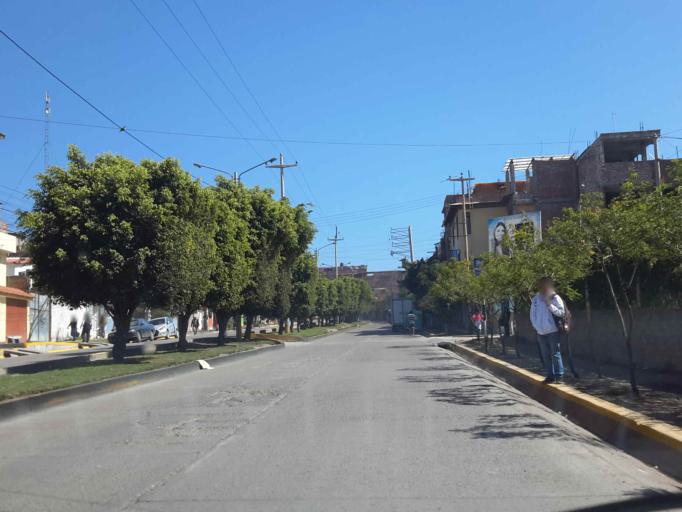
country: PE
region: Ayacucho
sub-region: Provincia de Huamanga
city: Ayacucho
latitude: -13.1457
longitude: -74.2250
